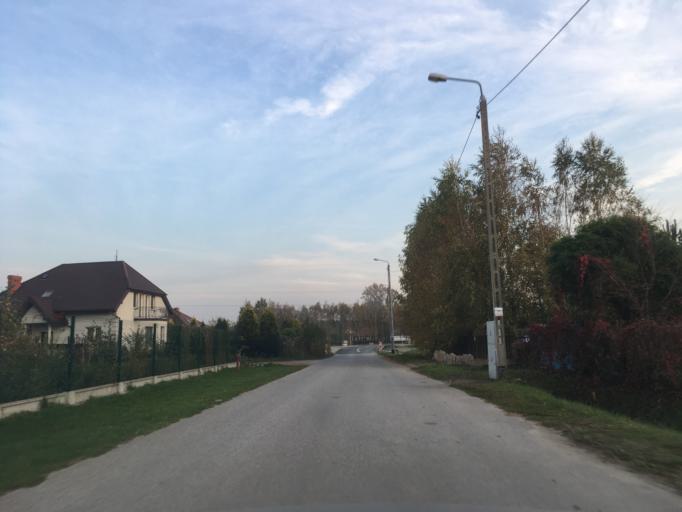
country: PL
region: Masovian Voivodeship
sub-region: Powiat piaseczynski
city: Lesznowola
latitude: 52.0481
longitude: 20.9295
